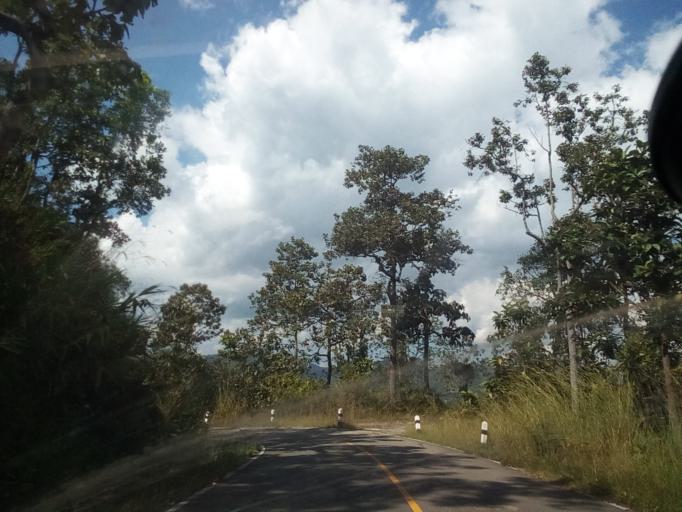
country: TH
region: Chiang Mai
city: Samoeng
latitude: 18.8755
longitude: 98.6892
